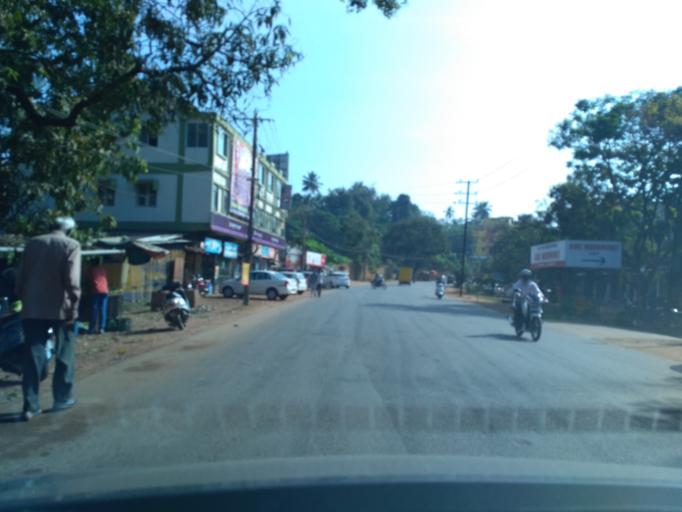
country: IN
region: Karnataka
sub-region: Dakshina Kannada
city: Mangalore
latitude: 12.8693
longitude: 74.8694
